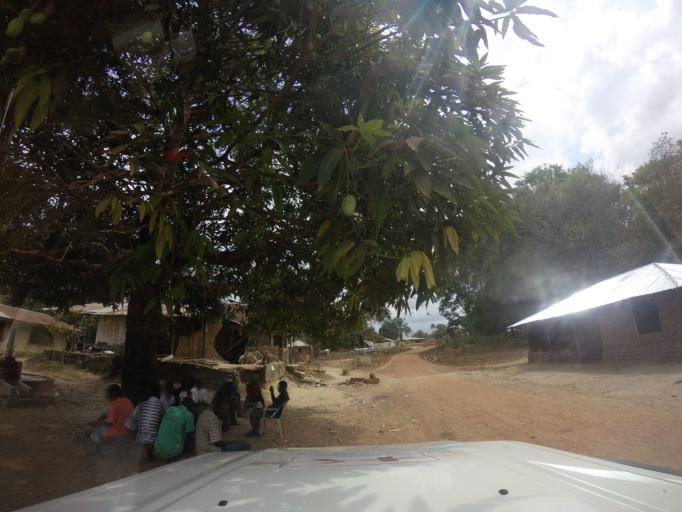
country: LR
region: Grand Cape Mount
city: Robertsport
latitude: 6.9224
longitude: -11.3880
